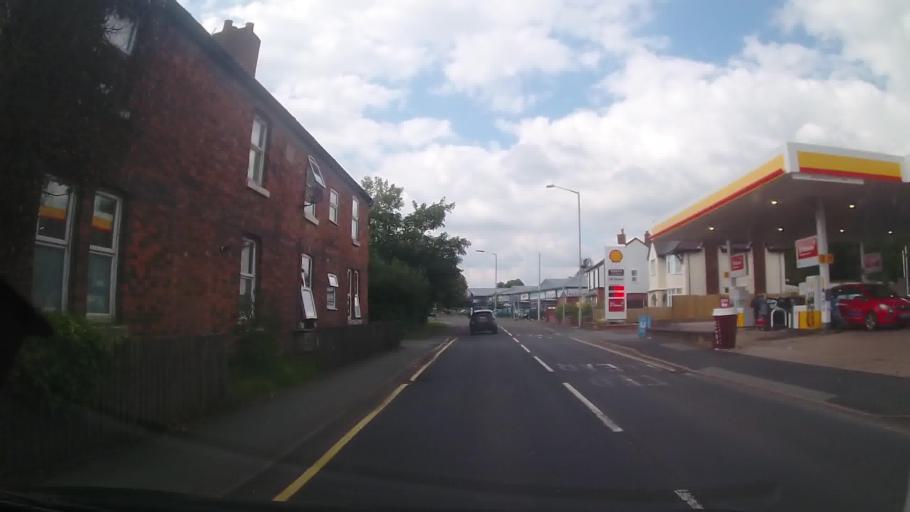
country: GB
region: England
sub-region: Shropshire
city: Oswestry
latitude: 52.8542
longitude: -3.0483
